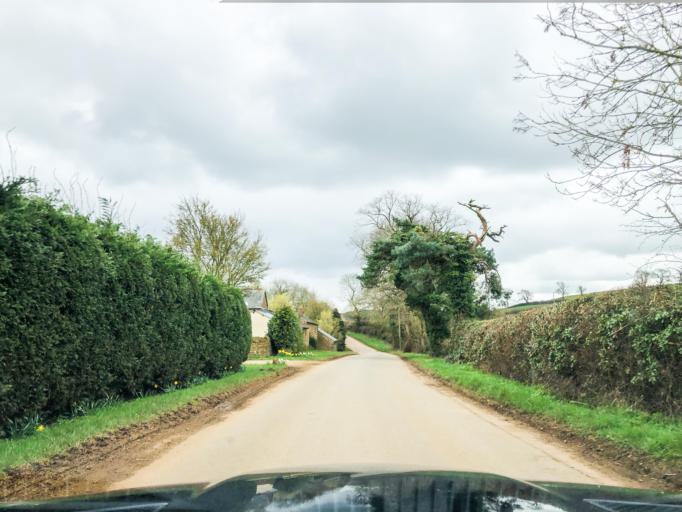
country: GB
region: England
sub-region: Oxfordshire
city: Hook Norton
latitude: 52.0740
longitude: -1.4770
